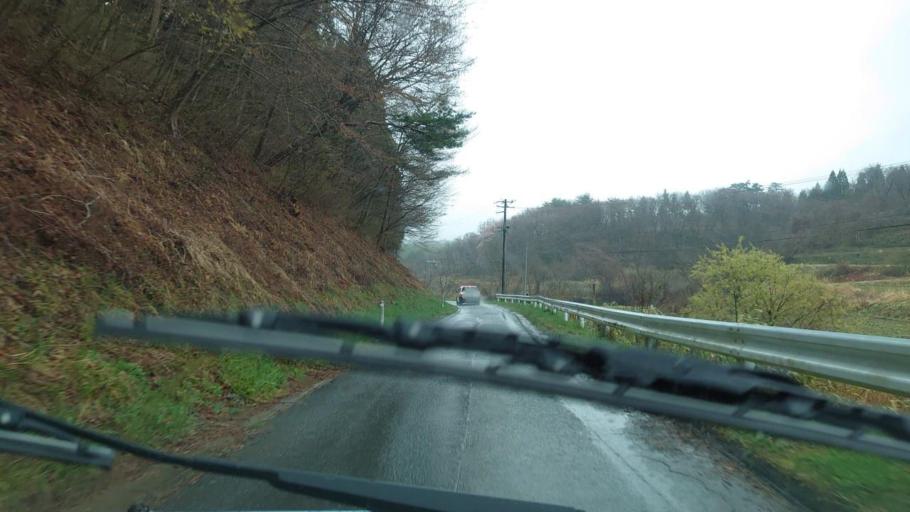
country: JP
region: Iwate
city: Ichinoseki
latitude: 38.8254
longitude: 141.3490
